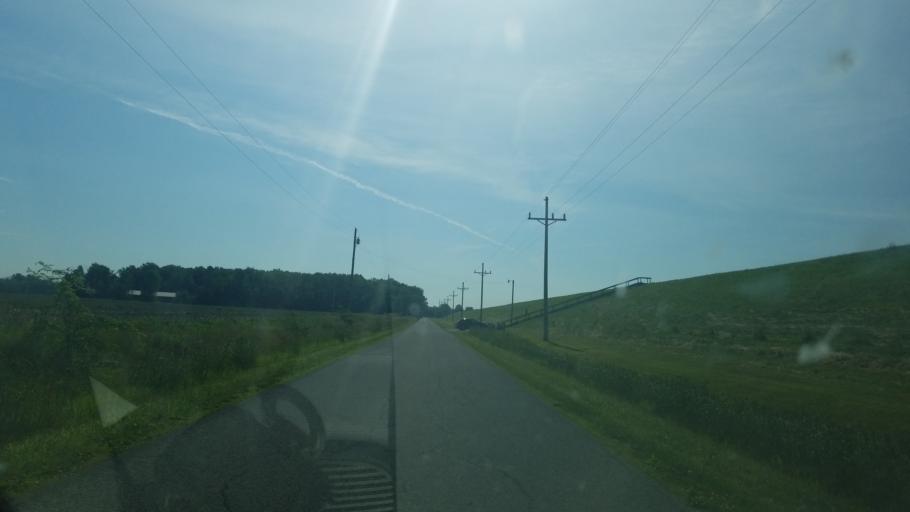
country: US
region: Ohio
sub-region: Hancock County
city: Findlay
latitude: 41.0290
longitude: -83.5765
